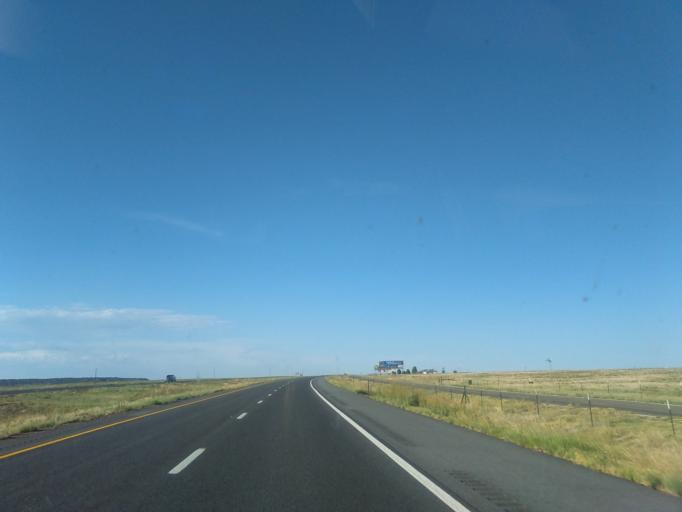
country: US
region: New Mexico
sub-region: San Miguel County
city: Las Vegas
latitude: 35.6664
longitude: -105.1839
